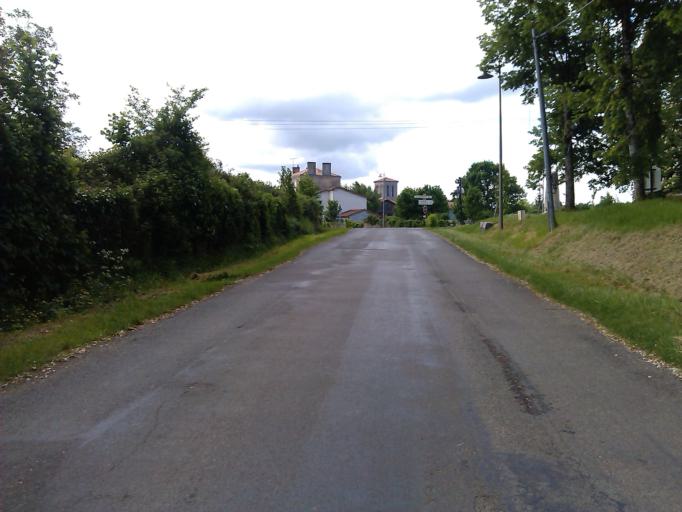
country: FR
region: Poitou-Charentes
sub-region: Departement de la Charente
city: Champagne-Mouton
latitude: 46.0407
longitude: 0.4537
